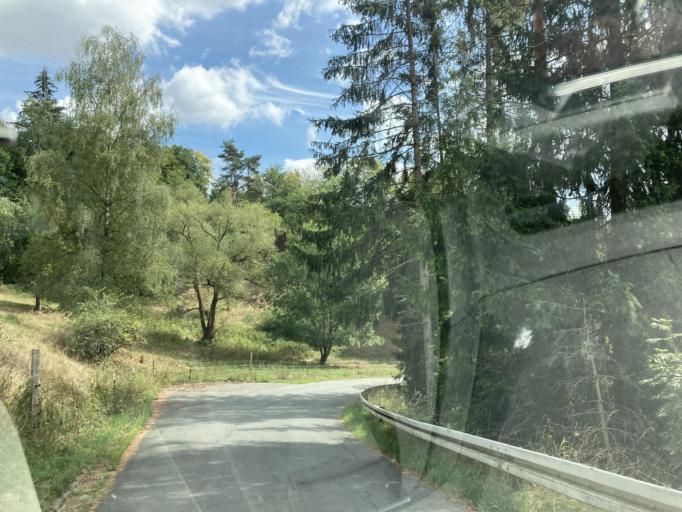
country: DE
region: Bavaria
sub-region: Upper Franconia
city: Presseck
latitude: 50.1948
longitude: 11.5595
